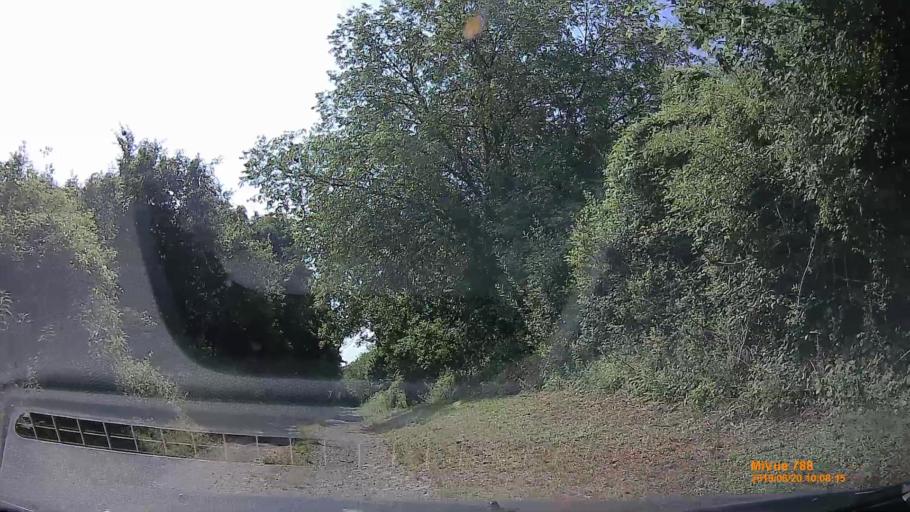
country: HU
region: Baranya
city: Mecseknadasd
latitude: 46.1802
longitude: 18.4801
